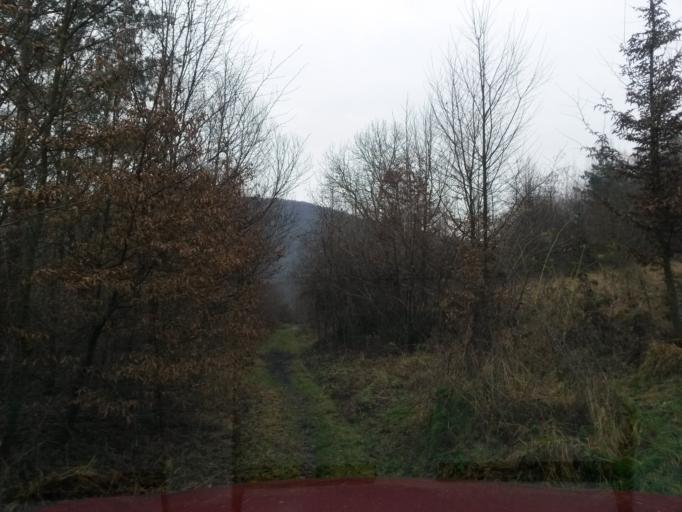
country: SK
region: Kosicky
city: Dobsina
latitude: 48.7422
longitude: 20.4126
